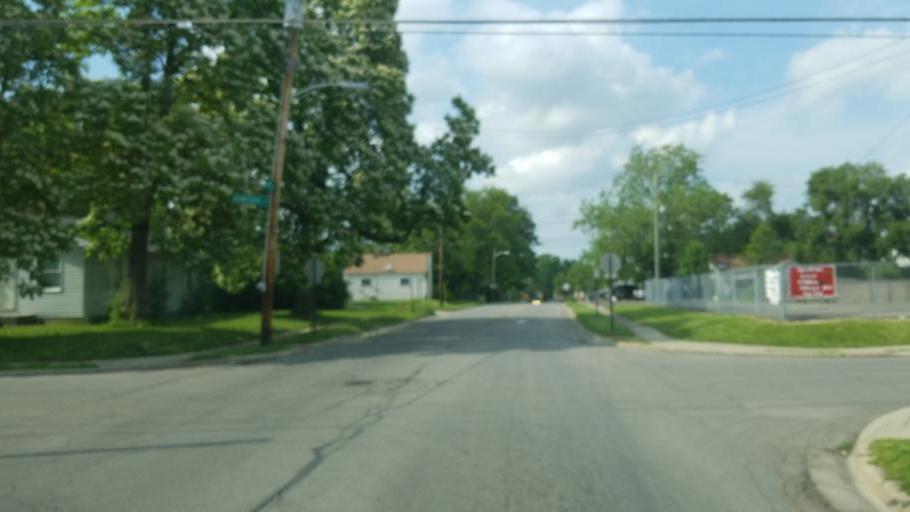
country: US
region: Ohio
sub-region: Franklin County
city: Bexley
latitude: 40.0186
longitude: -82.9608
